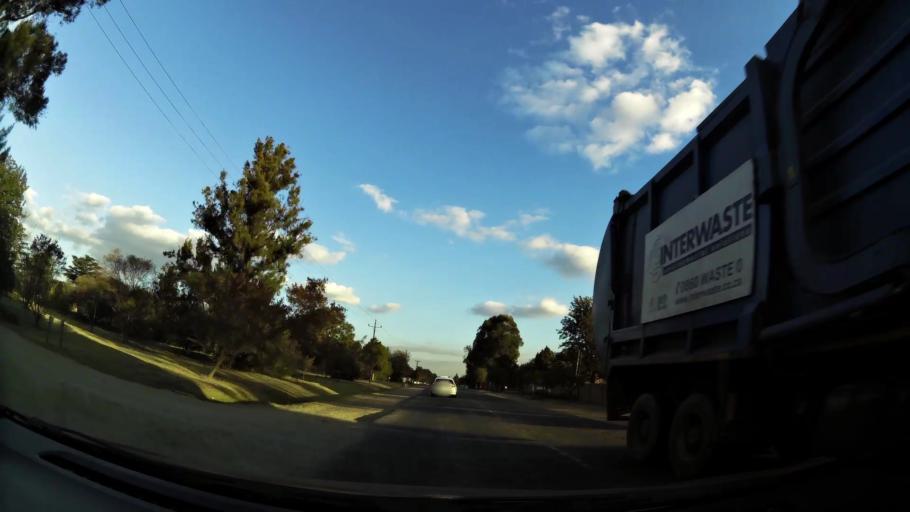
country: ZA
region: Gauteng
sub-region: City of Johannesburg Metropolitan Municipality
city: Midrand
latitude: -25.9712
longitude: 28.1534
